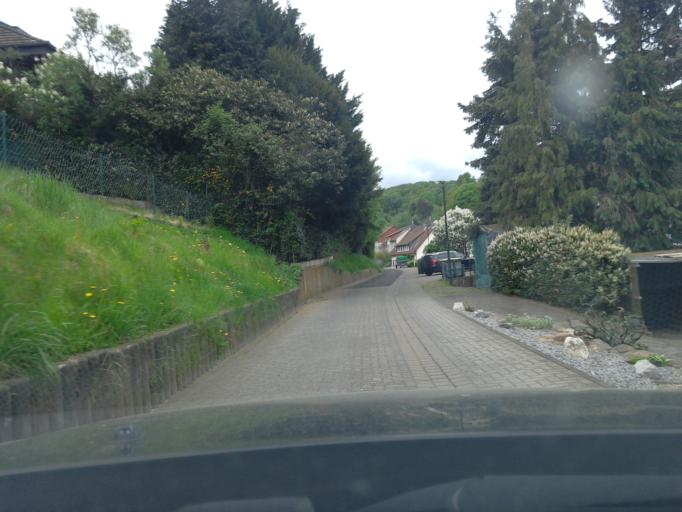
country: DE
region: Hesse
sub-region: Regierungsbezirk Darmstadt
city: Bad Orb
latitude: 50.2255
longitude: 9.3385
